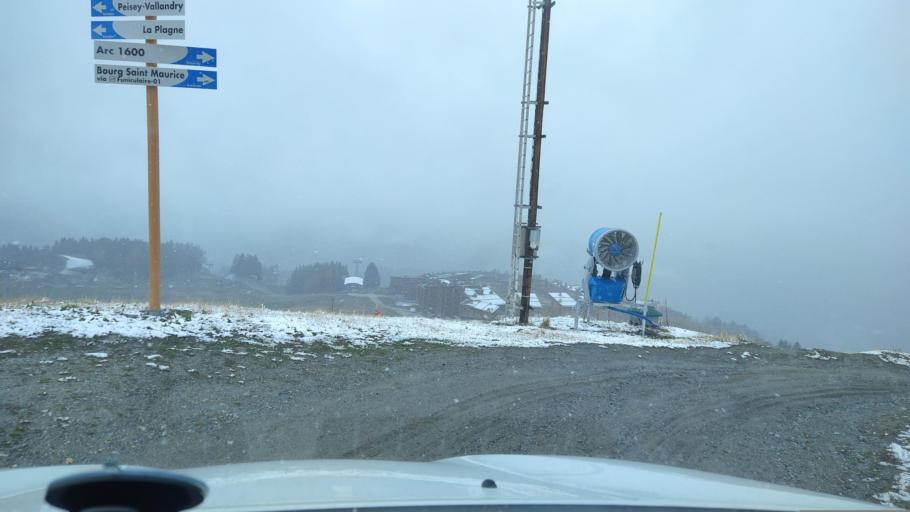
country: FR
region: Rhone-Alpes
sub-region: Departement de la Savoie
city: Bourg-Saint-Maurice
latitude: 45.5726
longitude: 6.7918
